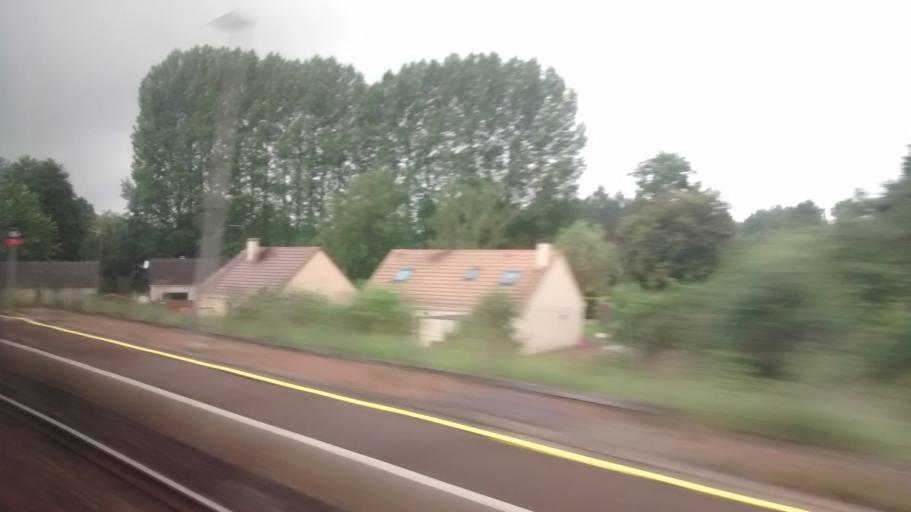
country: FR
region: Pays de la Loire
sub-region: Departement de la Sarthe
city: Saint-Mars-la-Briere
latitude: 48.0282
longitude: 0.3638
